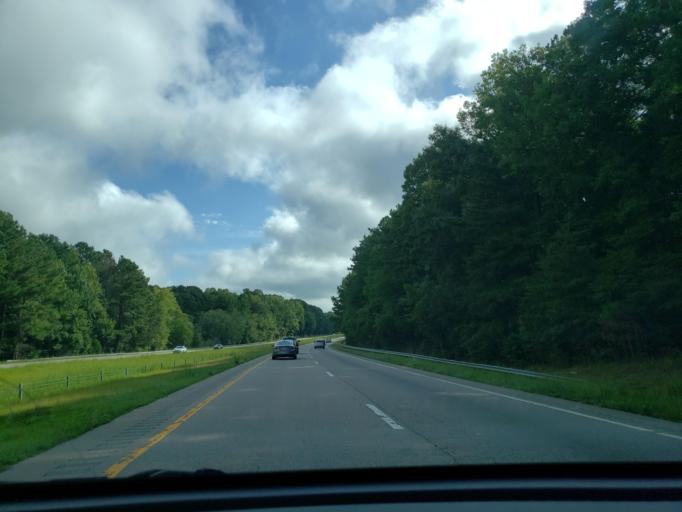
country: US
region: North Carolina
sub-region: Wake County
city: Zebulon
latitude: 35.8555
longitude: -78.2810
